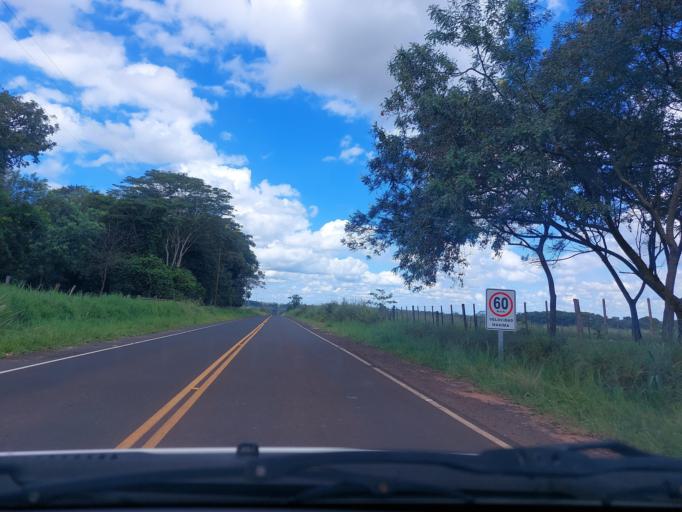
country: PY
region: San Pedro
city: Guayaybi
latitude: -24.5334
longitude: -56.5197
